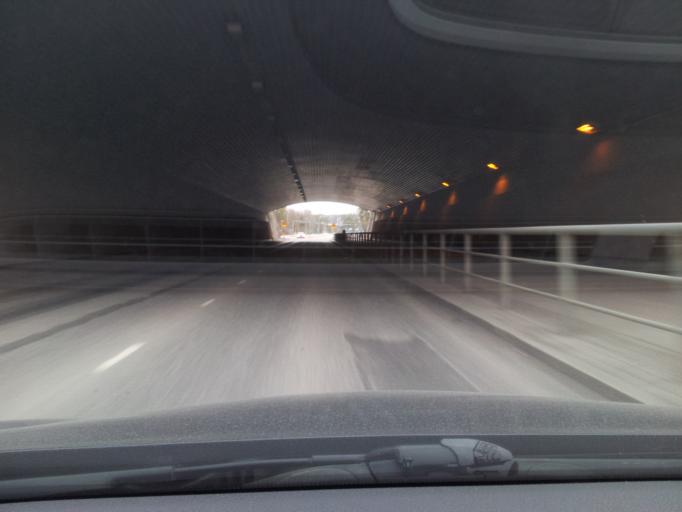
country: FI
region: Uusimaa
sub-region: Helsinki
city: Espoo
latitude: 60.1582
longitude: 24.6607
